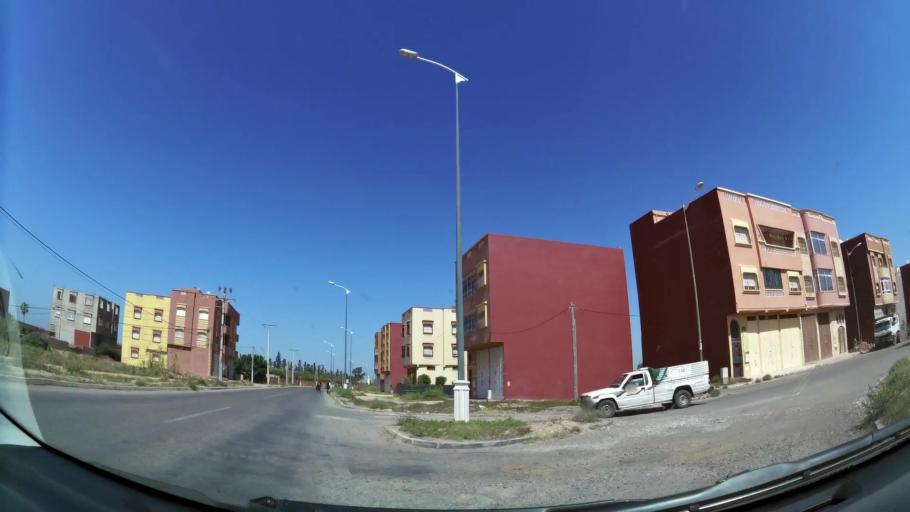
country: MA
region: Souss-Massa-Draa
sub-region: Inezgane-Ait Mellou
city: Inezgane
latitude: 30.3282
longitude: -9.5102
